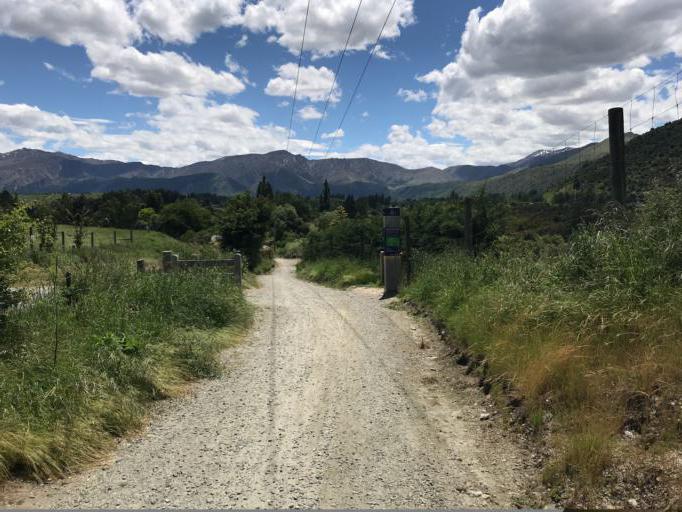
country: NZ
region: Otago
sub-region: Queenstown-Lakes District
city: Arrowtown
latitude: -44.9930
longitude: 168.8554
